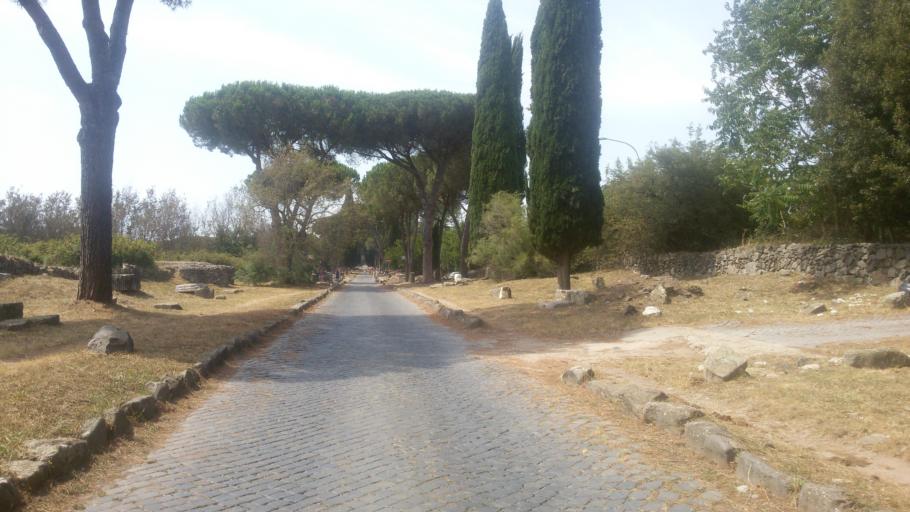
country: IT
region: Latium
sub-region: Citta metropolitana di Roma Capitale
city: Rome
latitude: 41.8337
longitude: 12.5412
